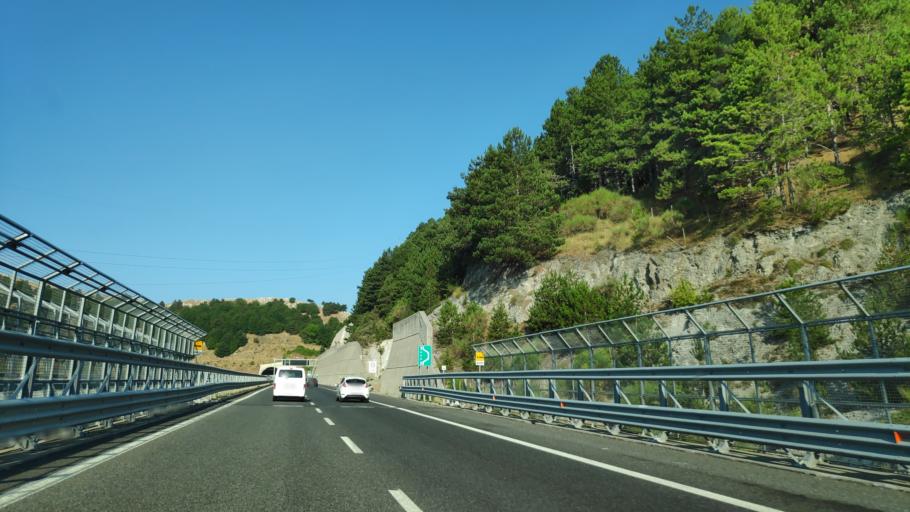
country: IT
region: Calabria
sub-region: Provincia di Cosenza
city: Morano Calabro
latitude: 39.8678
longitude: 16.1039
